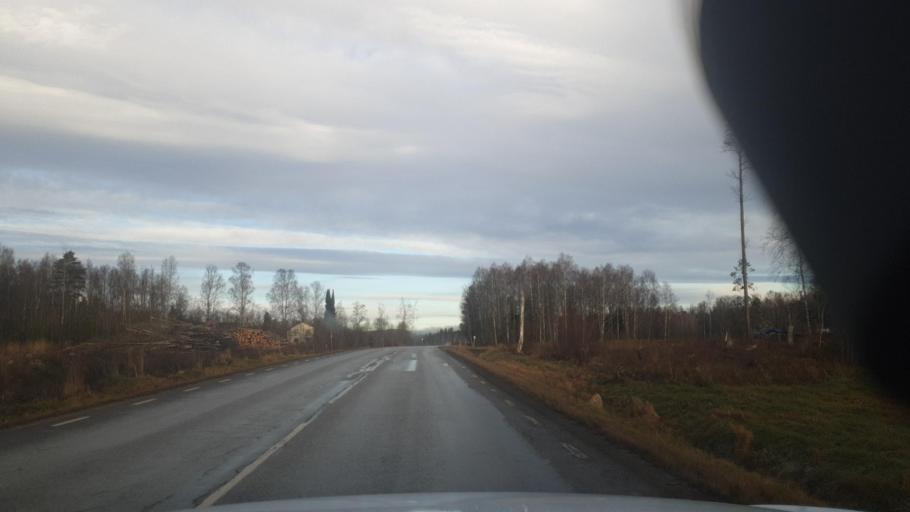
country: SE
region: Vaermland
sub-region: Arvika Kommun
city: Arvika
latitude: 59.6903
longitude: 12.6334
